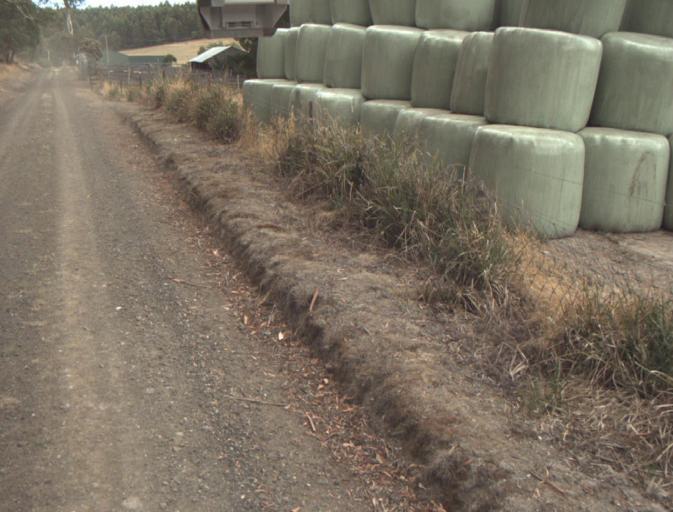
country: AU
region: Tasmania
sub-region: Launceston
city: Mayfield
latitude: -41.2388
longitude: 147.1863
